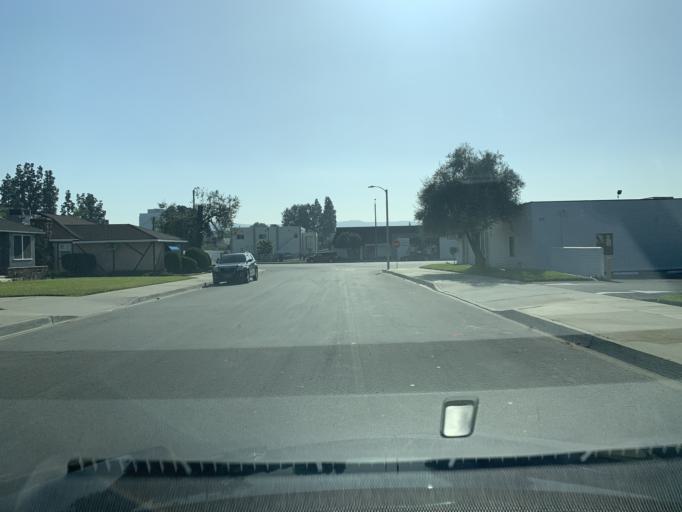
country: US
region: California
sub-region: Los Angeles County
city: Covina
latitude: 34.0796
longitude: -117.8835
